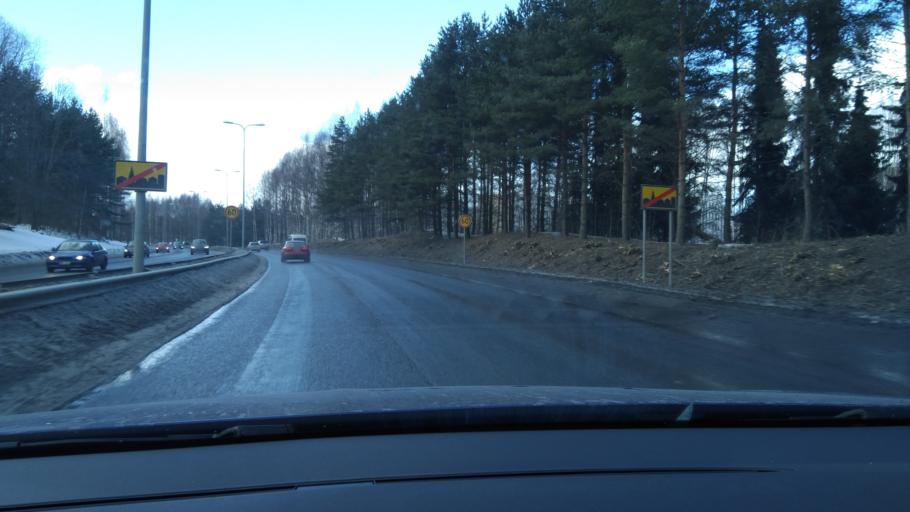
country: FI
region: Pirkanmaa
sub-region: Tampere
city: Tampere
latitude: 61.4963
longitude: 23.8186
